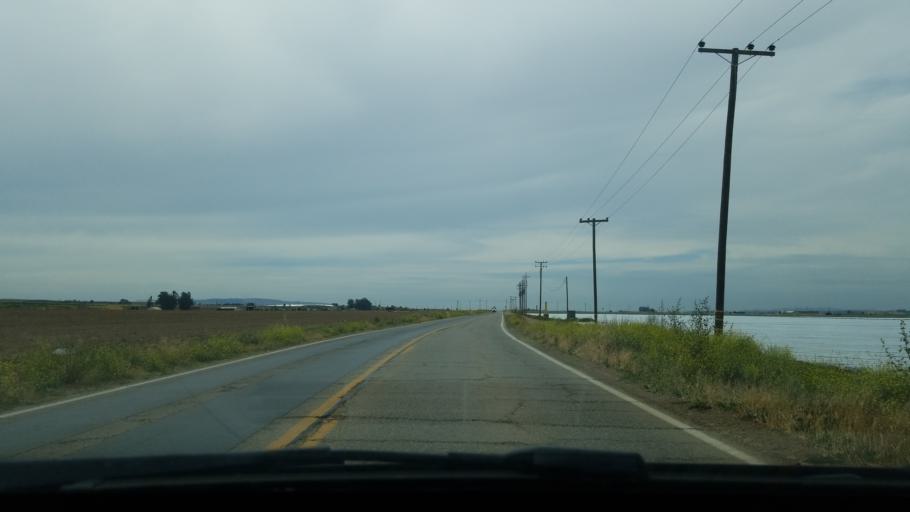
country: US
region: California
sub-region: Santa Barbara County
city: Orcutt
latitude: 34.9065
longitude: -120.3214
